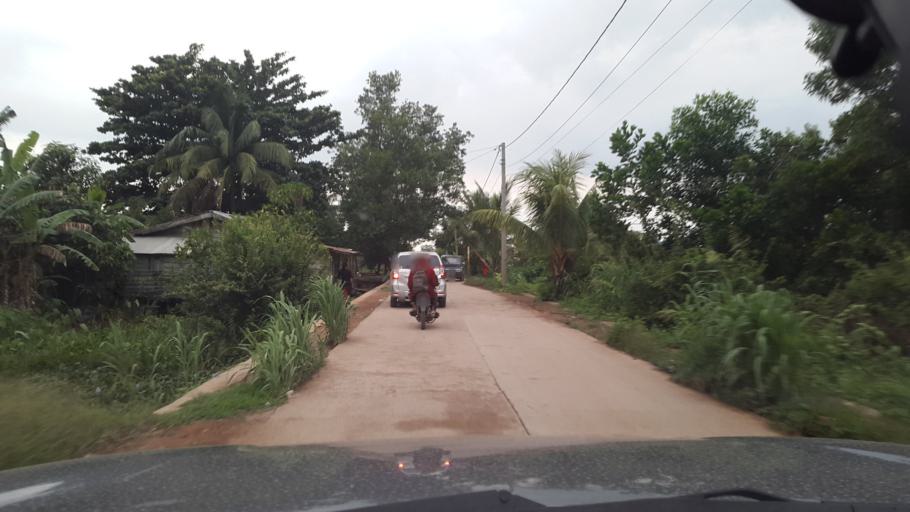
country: ID
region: South Sumatra
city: Plaju
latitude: -3.0542
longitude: 104.7900
